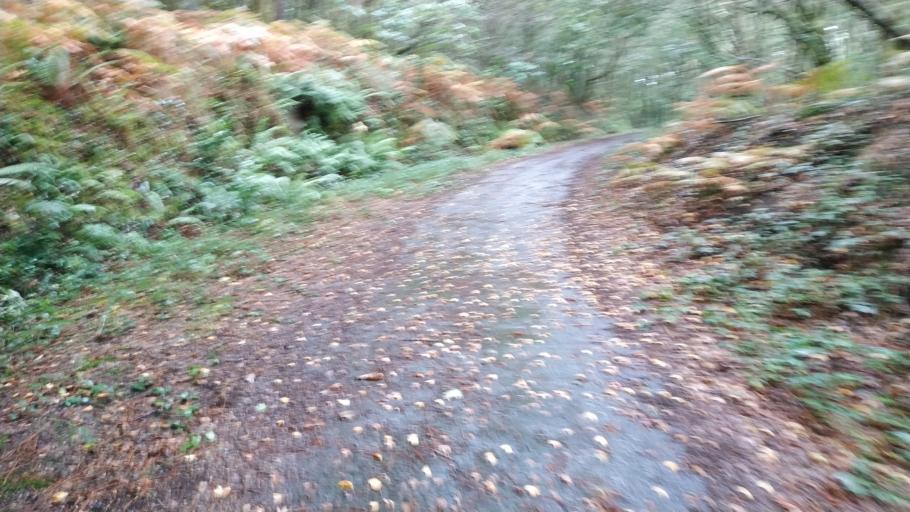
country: ES
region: Galicia
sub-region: Provincia da Coruna
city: Negreira
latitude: 42.9115
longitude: -8.7497
